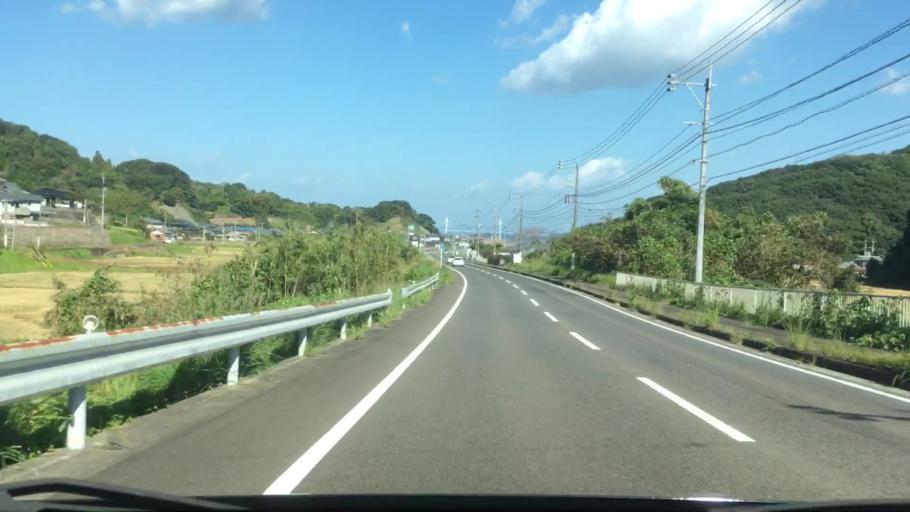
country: JP
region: Nagasaki
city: Sasebo
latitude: 32.9840
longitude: 129.6460
